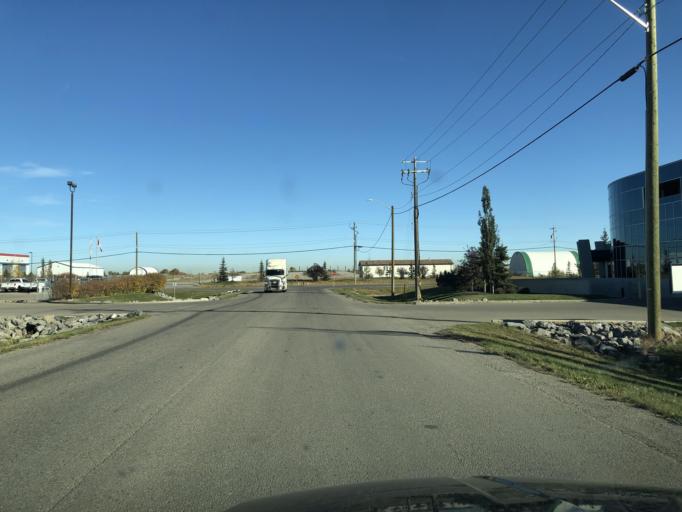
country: CA
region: Alberta
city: Chestermere
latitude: 50.9693
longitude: -113.9026
